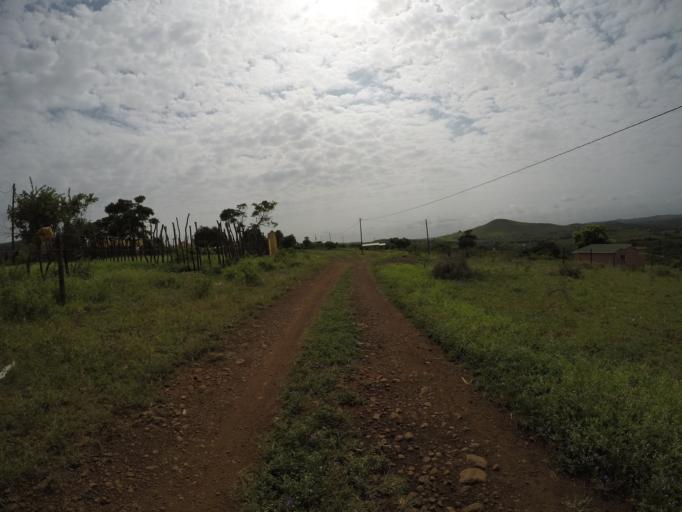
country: ZA
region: KwaZulu-Natal
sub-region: uThungulu District Municipality
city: Empangeni
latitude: -28.6198
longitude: 31.9057
